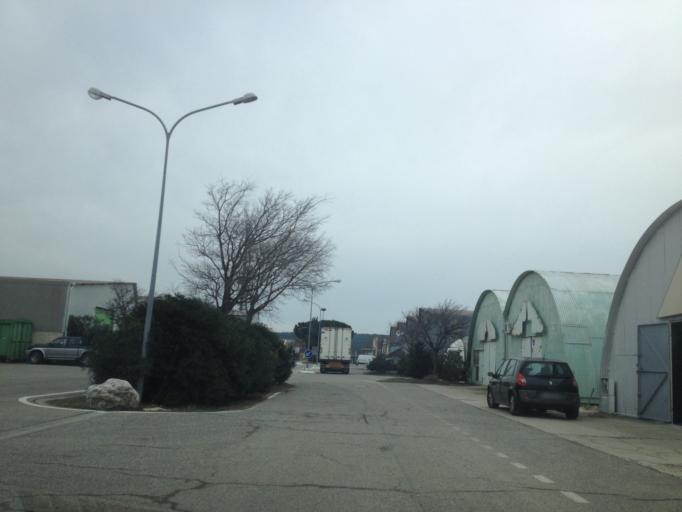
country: FR
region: Provence-Alpes-Cote d'Azur
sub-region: Departement du Vaucluse
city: Sorgues
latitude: 44.0286
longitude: 4.8719
